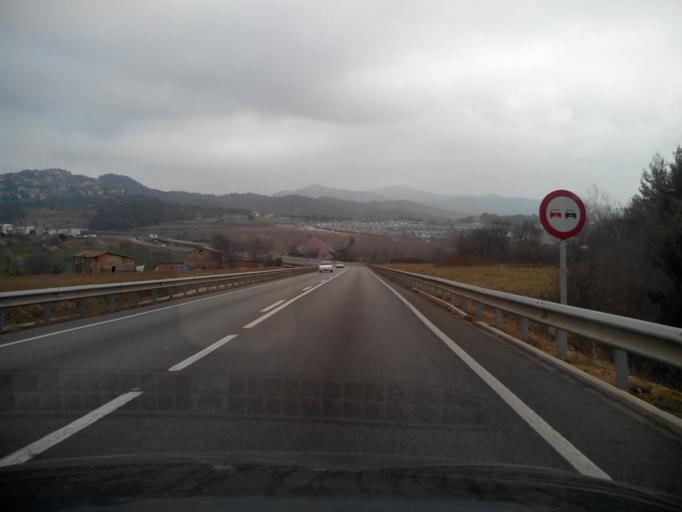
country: ES
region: Catalonia
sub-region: Provincia de Barcelona
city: Berga
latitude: 42.0921
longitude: 1.8429
